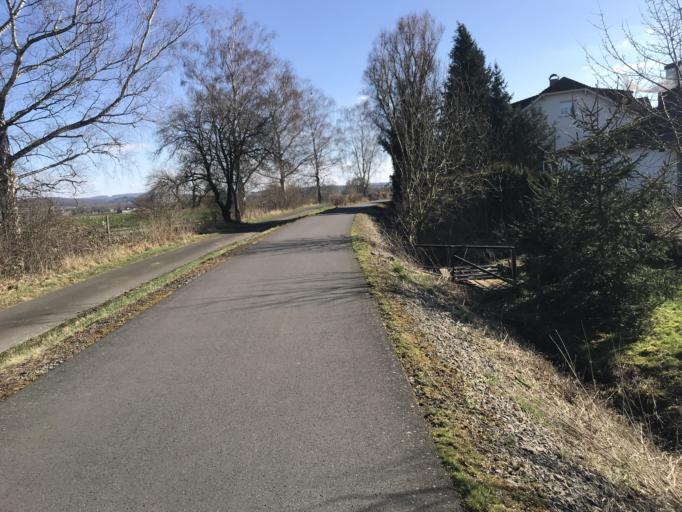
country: DE
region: Hesse
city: Schwalmstadt
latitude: 50.9042
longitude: 9.2355
